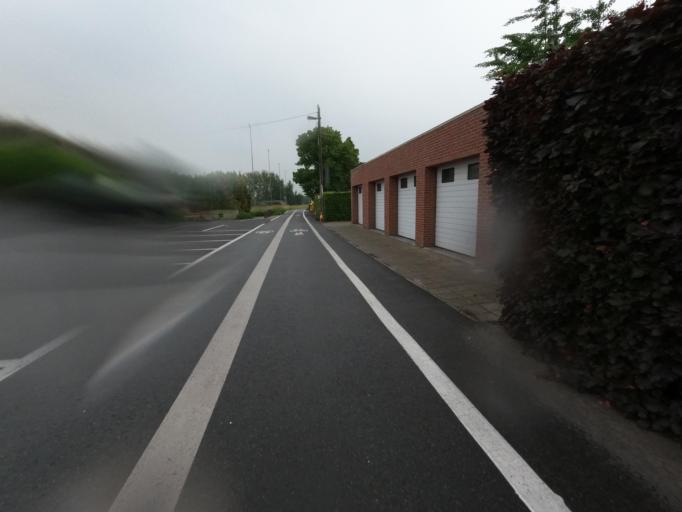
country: BE
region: Flanders
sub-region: Provincie Antwerpen
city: Essen
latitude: 51.4318
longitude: 4.5144
